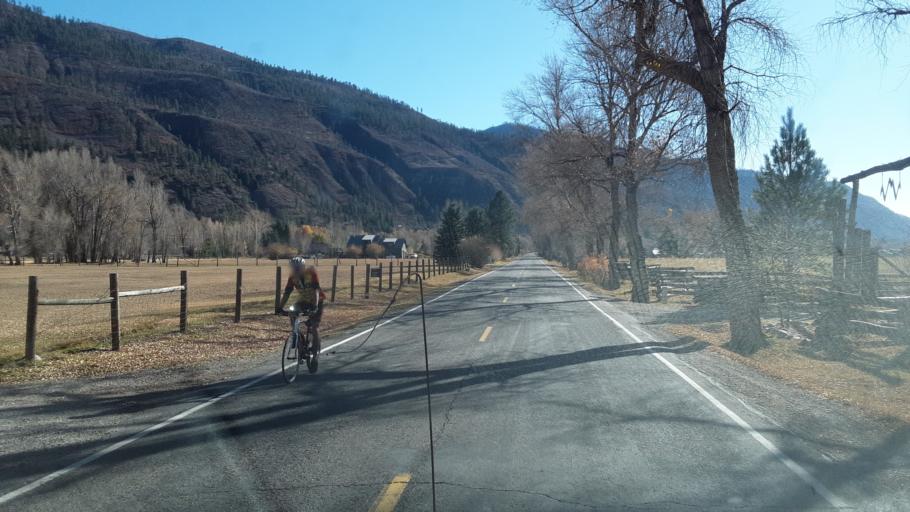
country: US
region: Colorado
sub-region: La Plata County
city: Durango
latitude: 37.4306
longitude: -107.7996
